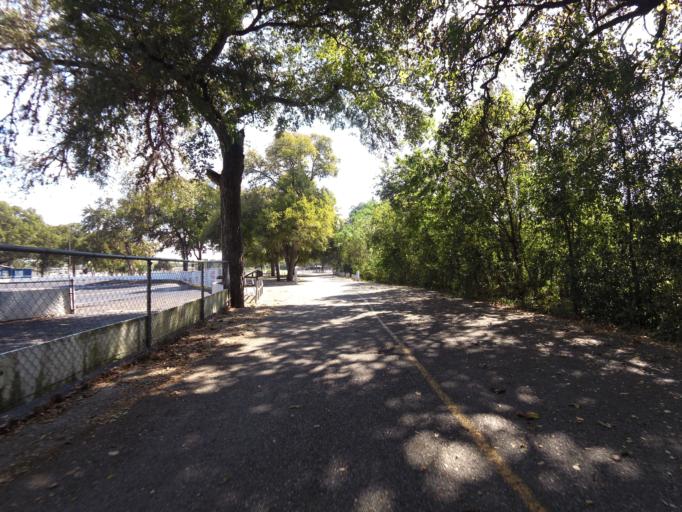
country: US
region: Texas
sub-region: Bexar County
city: China Grove
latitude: 29.3990
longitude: -98.4204
